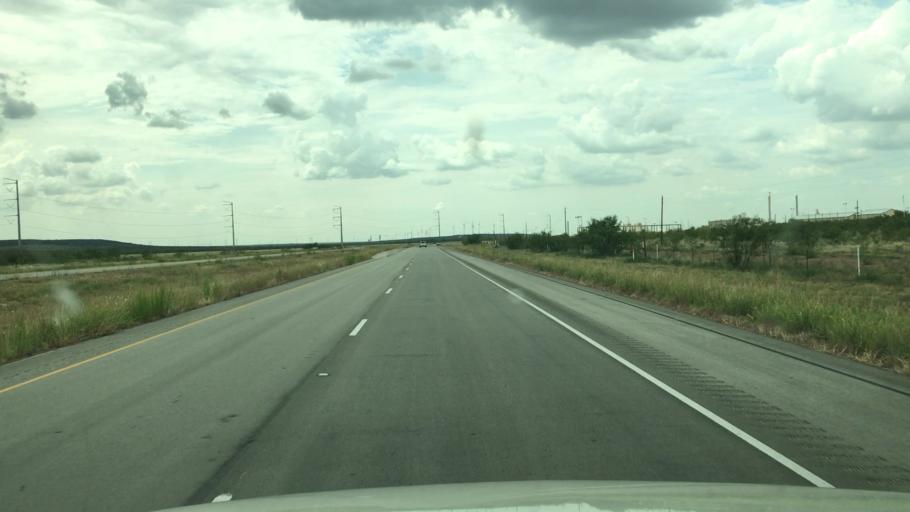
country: US
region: Texas
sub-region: Glasscock County
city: Garden City
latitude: 31.9670
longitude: -101.2332
